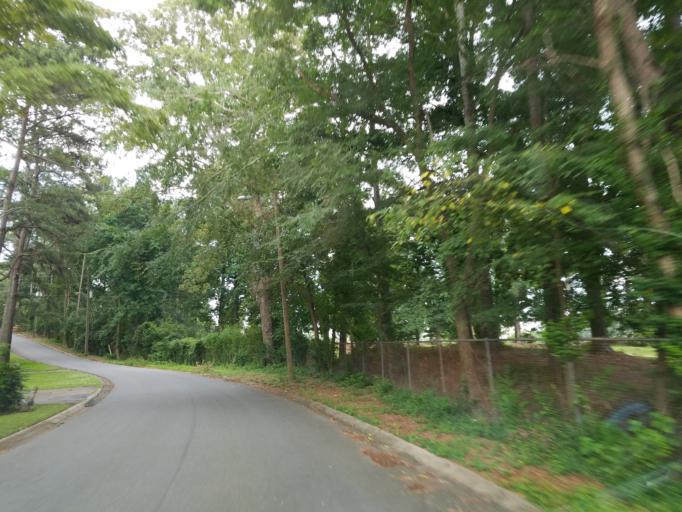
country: US
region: Georgia
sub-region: Cobb County
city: Marietta
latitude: 33.9455
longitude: -84.5605
